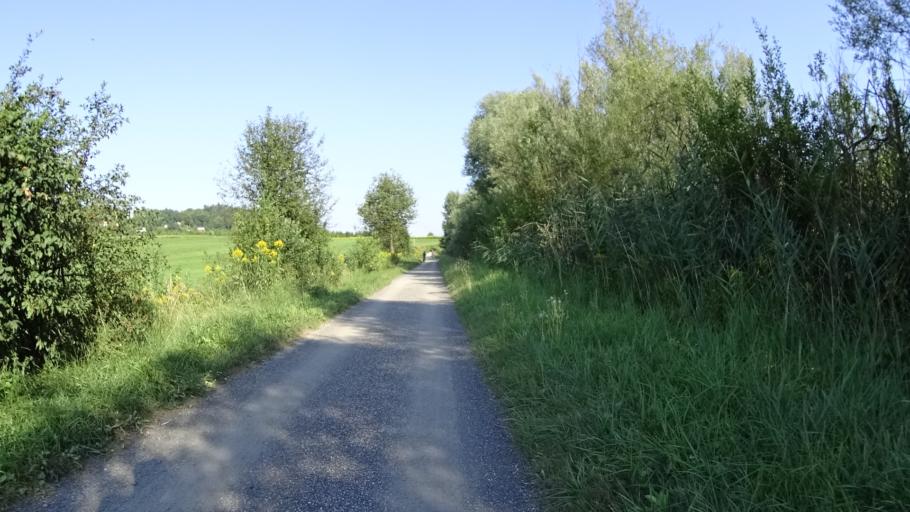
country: AT
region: Carinthia
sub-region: Politischer Bezirk Villach Land
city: Wernberg
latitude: 46.6045
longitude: 13.9436
